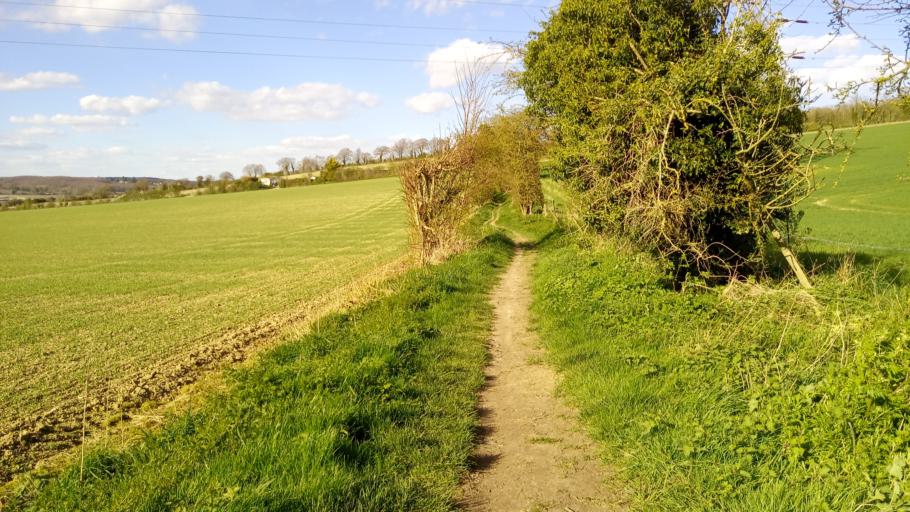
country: GB
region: England
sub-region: Kent
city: Chartham
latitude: 51.2506
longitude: 1.0361
